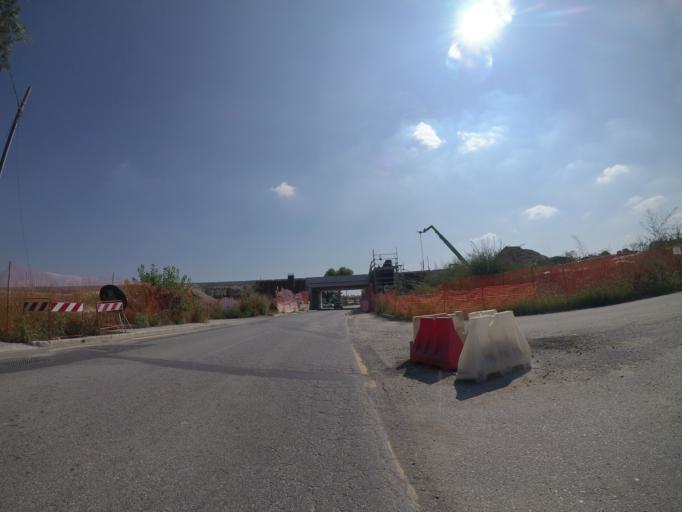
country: IT
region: Friuli Venezia Giulia
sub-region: Provincia di Udine
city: Pocenia
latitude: 45.8317
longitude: 13.0999
